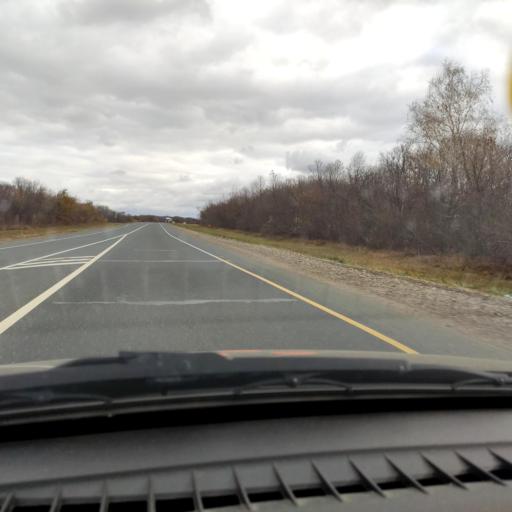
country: RU
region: Samara
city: Mezhdurechensk
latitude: 53.2588
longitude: 49.0777
